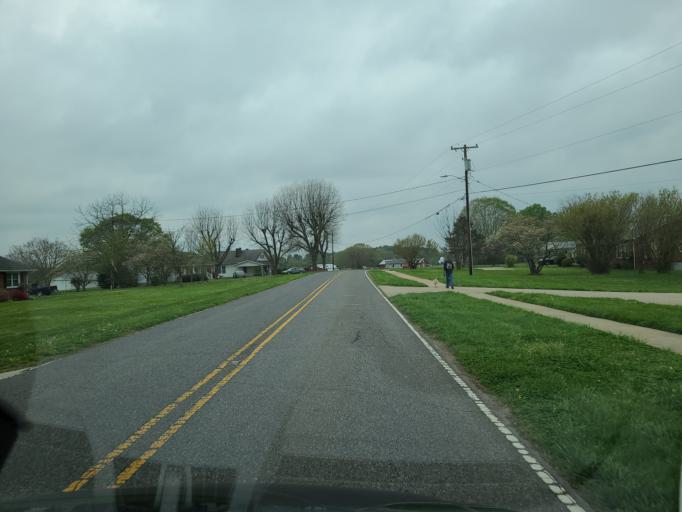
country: US
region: North Carolina
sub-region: Gaston County
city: Cherryville
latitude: 35.4243
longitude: -81.4911
